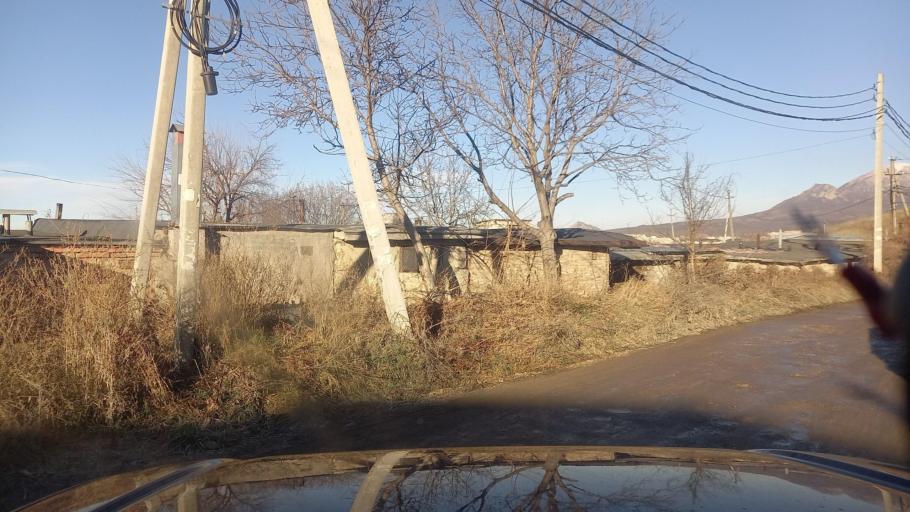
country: RU
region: Stavropol'skiy
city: Svobody
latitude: 44.0201
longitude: 43.0519
